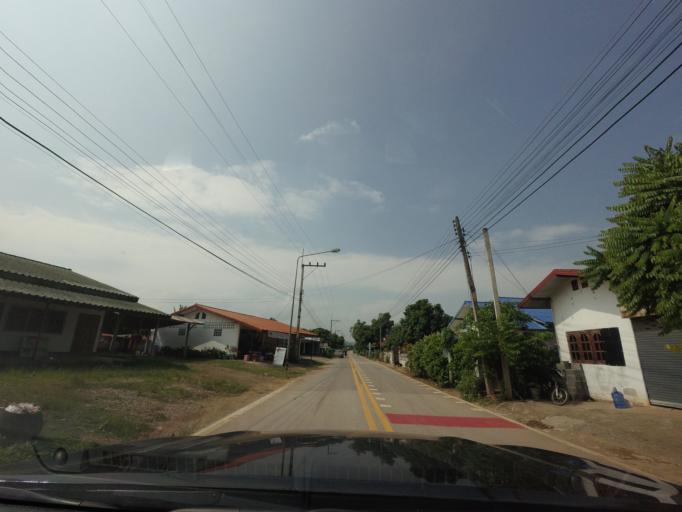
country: LA
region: Xiagnabouli
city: Muang Kenthao
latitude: 17.7035
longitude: 101.4125
